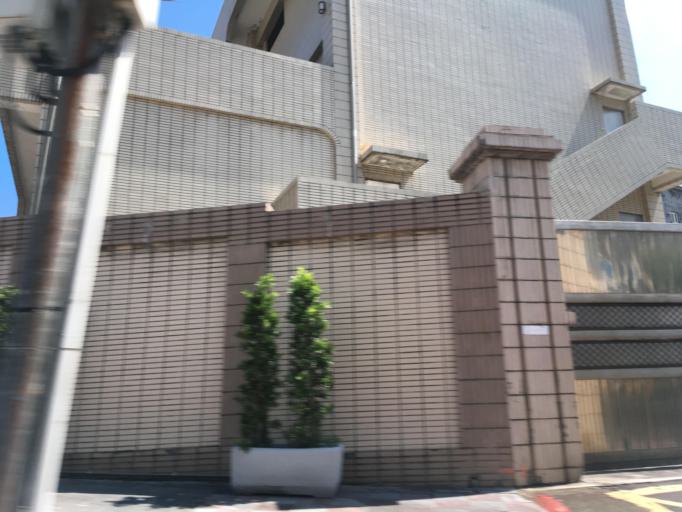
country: TW
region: Taipei
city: Taipei
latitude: 25.1425
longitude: 121.5004
